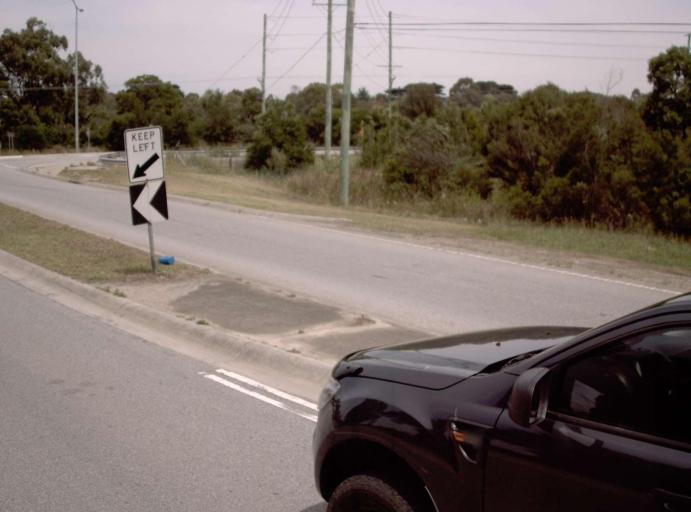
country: AU
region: Victoria
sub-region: Mornington Peninsula
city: Tyabb
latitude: -38.2716
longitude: 145.1907
